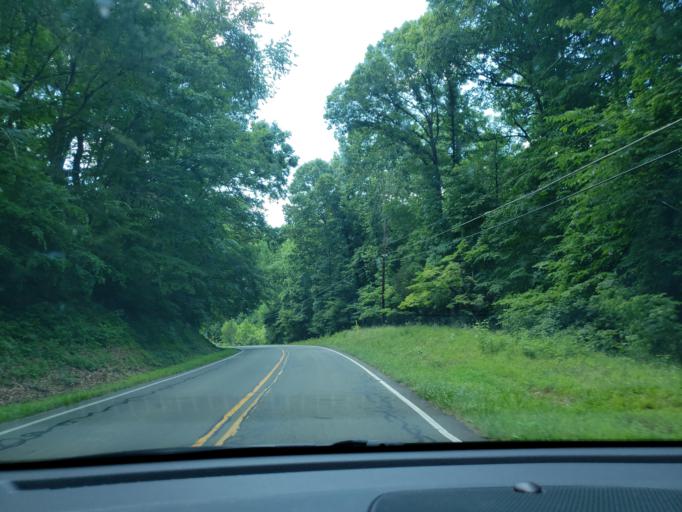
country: US
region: North Carolina
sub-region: Orange County
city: Chapel Hill
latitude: 35.9921
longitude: -79.0007
